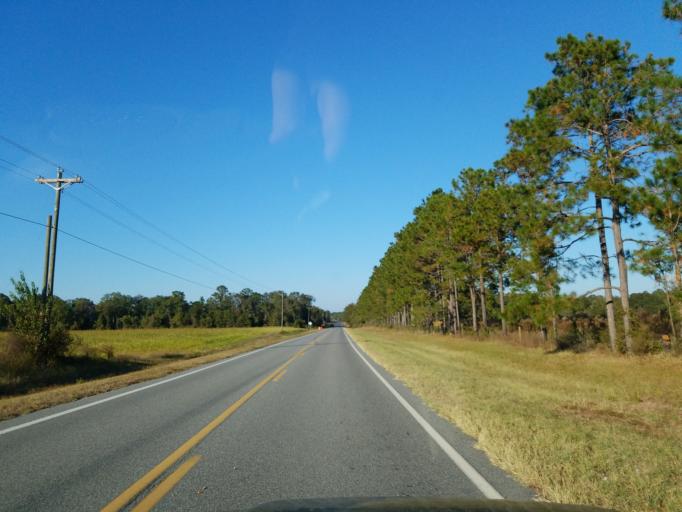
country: US
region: Georgia
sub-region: Echols County
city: Statenville
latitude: 30.6971
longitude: -83.0632
